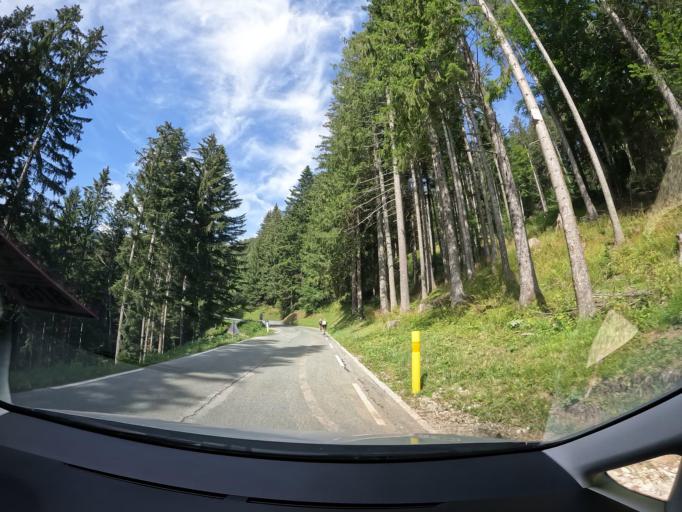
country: AT
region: Carinthia
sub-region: Politischer Bezirk Klagenfurt Land
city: Maria Saal
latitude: 46.6918
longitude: 14.3180
